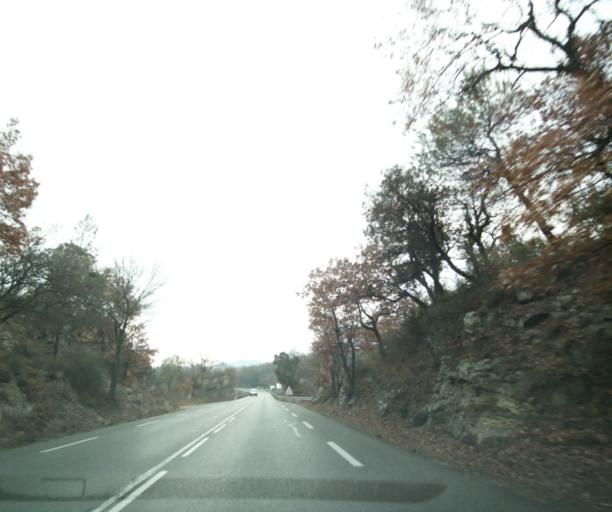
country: FR
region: Provence-Alpes-Cote d'Azur
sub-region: Departement du Var
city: Saint-Maximin-la-Sainte-Baume
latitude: 43.4307
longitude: 5.8854
